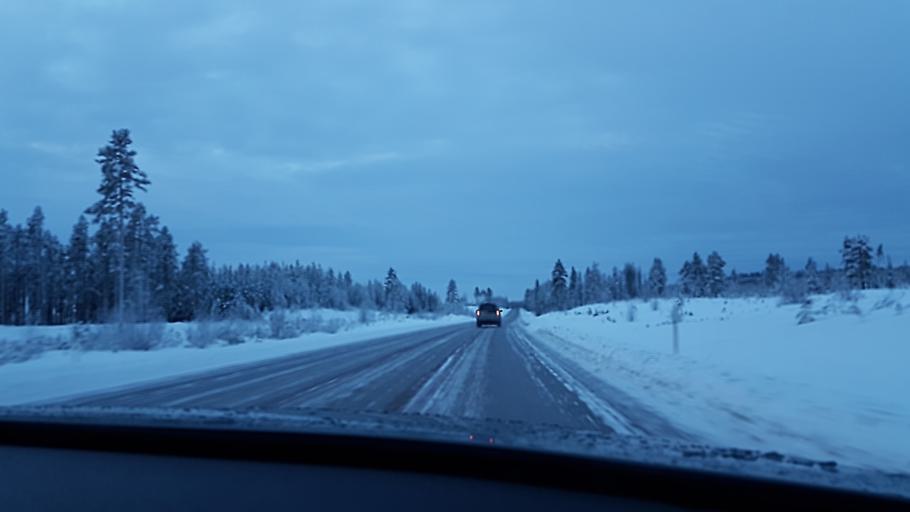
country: SE
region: Jaemtland
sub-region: Harjedalens Kommun
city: Sveg
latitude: 62.0434
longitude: 14.7532
